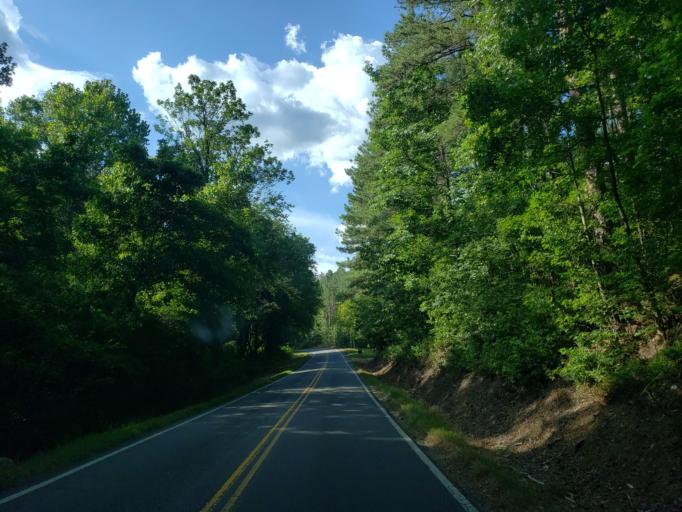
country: US
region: Georgia
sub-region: Floyd County
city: Lindale
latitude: 34.1873
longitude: -85.0572
